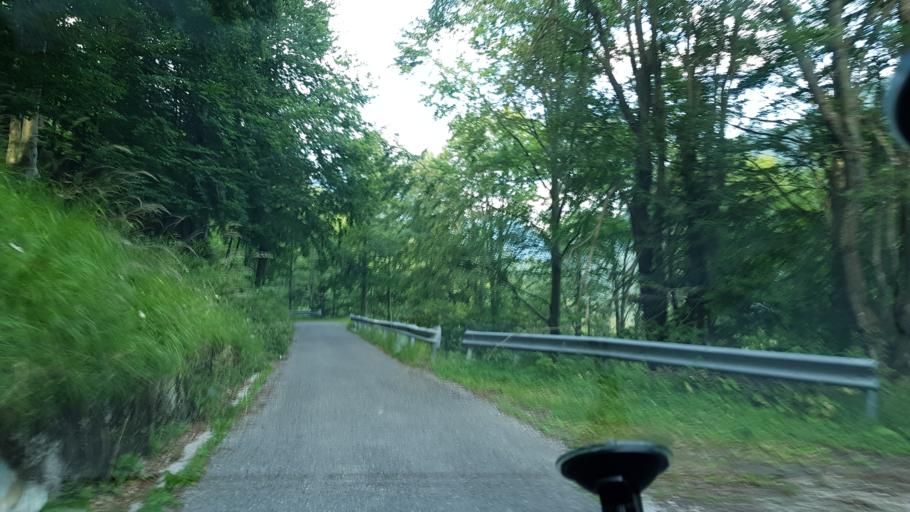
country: IT
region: Friuli Venezia Giulia
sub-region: Provincia di Udine
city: Prato
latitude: 46.3313
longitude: 13.3421
